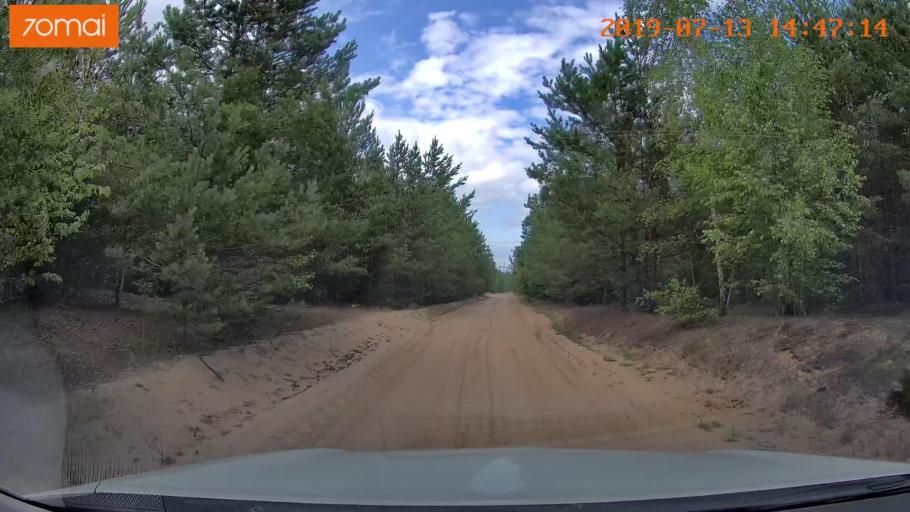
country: BY
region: Mogilev
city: Hlusha
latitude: 53.1994
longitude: 28.7541
